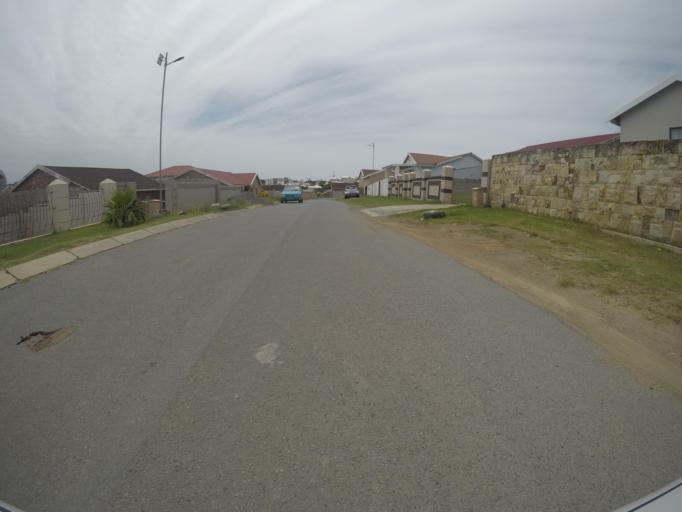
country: ZA
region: Eastern Cape
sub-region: Buffalo City Metropolitan Municipality
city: East London
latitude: -32.9606
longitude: 27.9300
